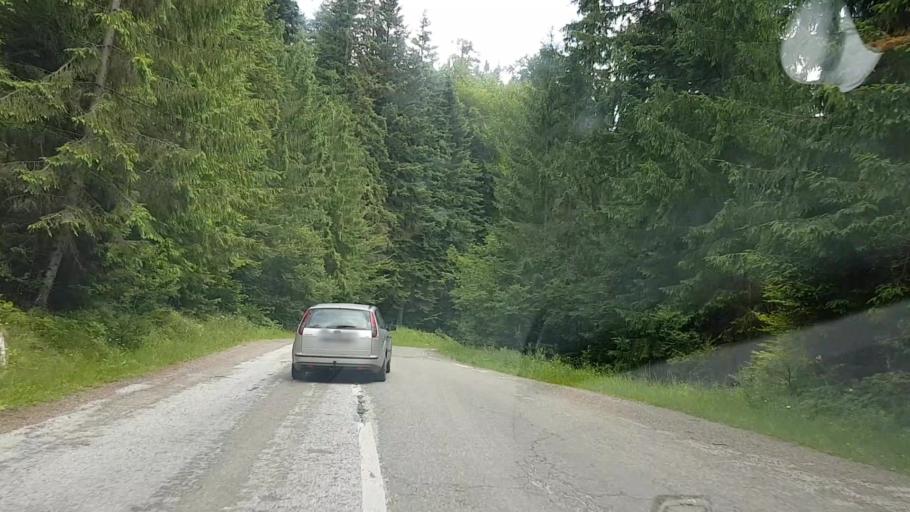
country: RO
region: Neamt
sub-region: Comuna Pangarati
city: Pangarati
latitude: 46.9710
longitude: 26.1172
